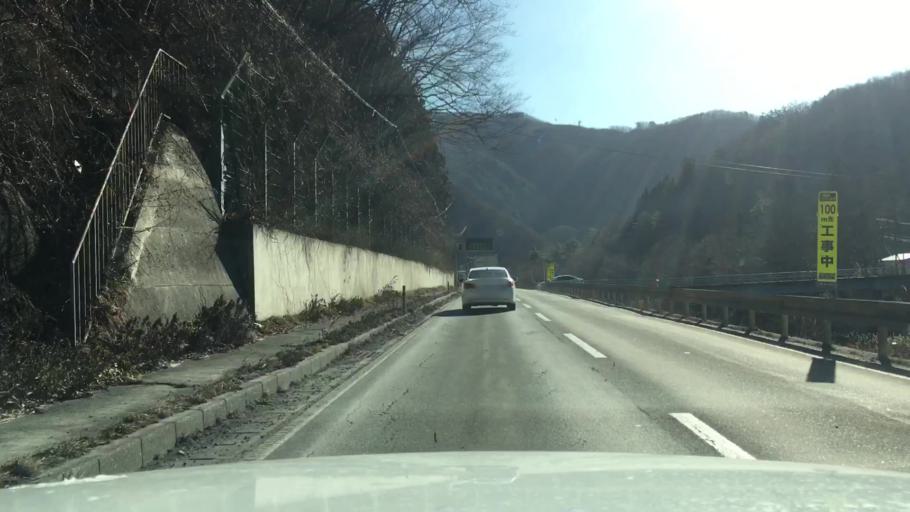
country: JP
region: Iwate
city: Miyako
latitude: 39.5960
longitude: 141.6588
